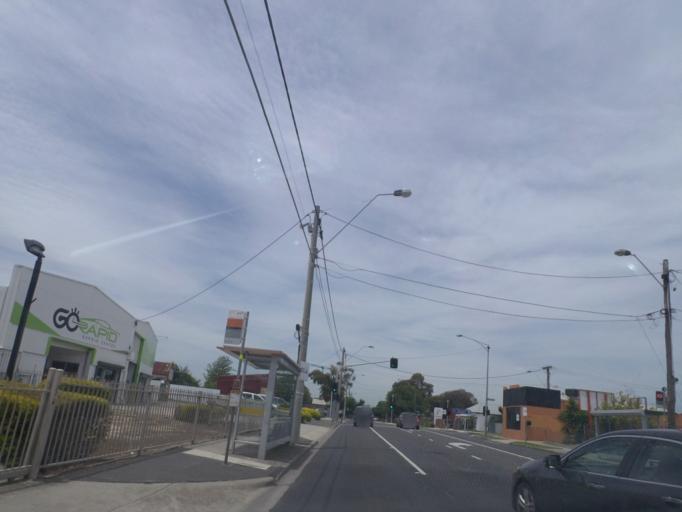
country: AU
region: Victoria
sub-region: Maribyrnong
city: Maribyrnong
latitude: -37.7894
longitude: 144.8855
